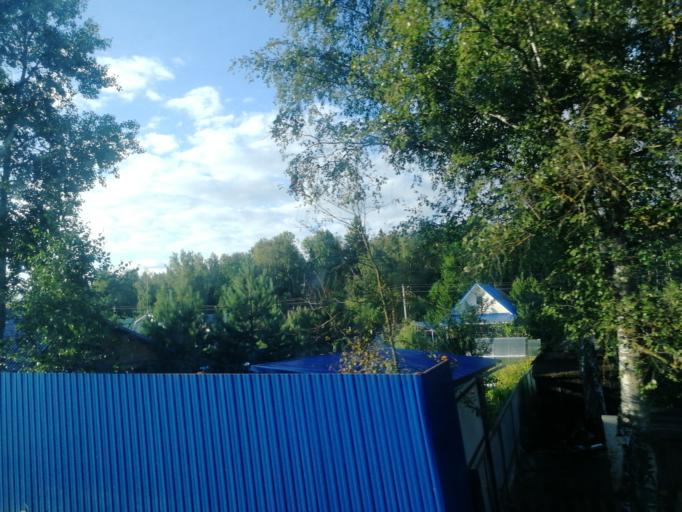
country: RU
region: Kaluga
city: Kaluga
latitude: 54.4521
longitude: 36.2960
